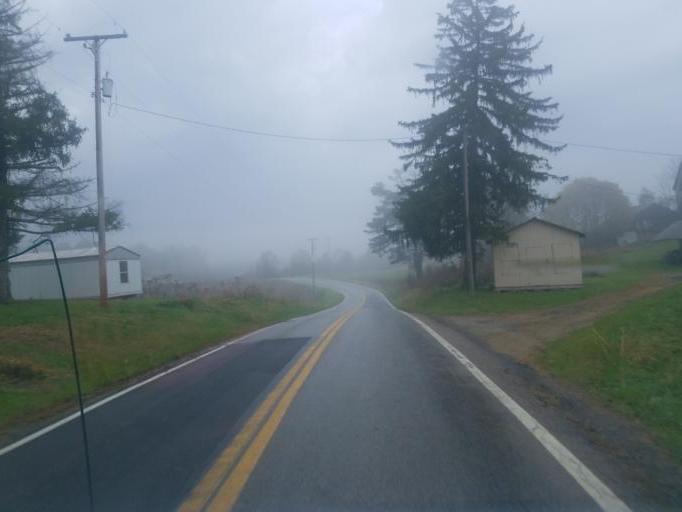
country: US
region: Ohio
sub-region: Morgan County
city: McConnelsville
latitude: 39.4984
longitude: -81.8950
